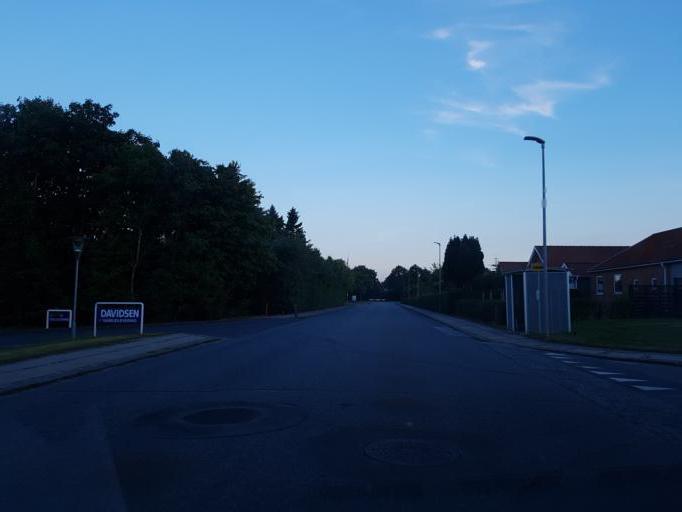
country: DK
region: South Denmark
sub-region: Vejen Kommune
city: Vejen
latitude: 55.4644
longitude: 9.1328
